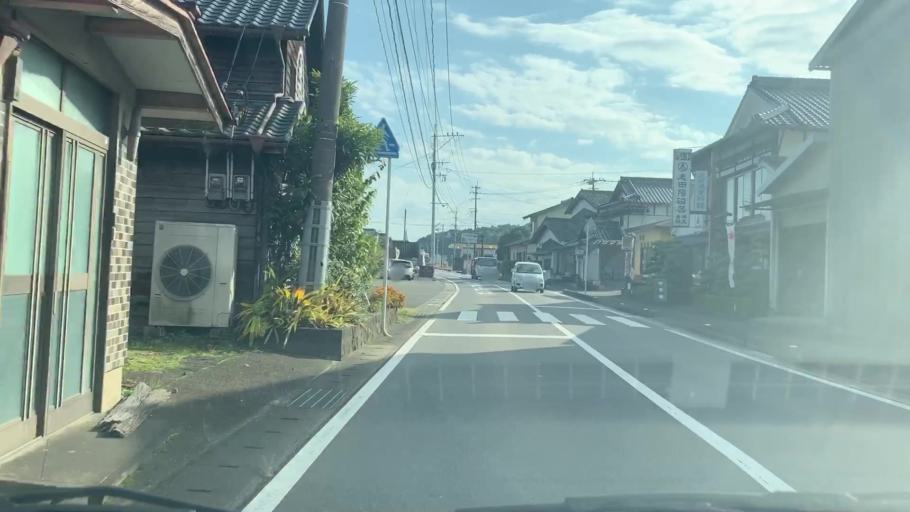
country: JP
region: Saga Prefecture
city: Takeocho-takeo
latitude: 33.1576
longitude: 130.0628
